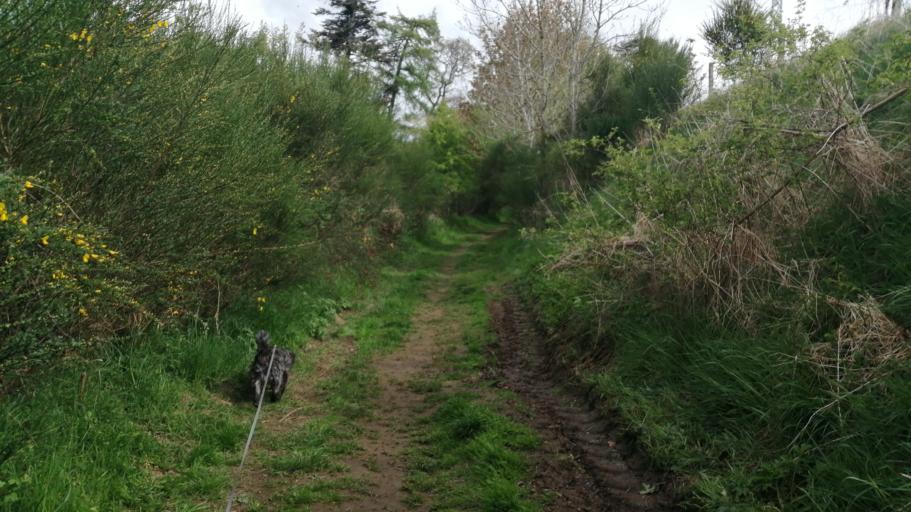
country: GB
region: Scotland
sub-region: Moray
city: Keith
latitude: 57.5316
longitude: -2.9626
